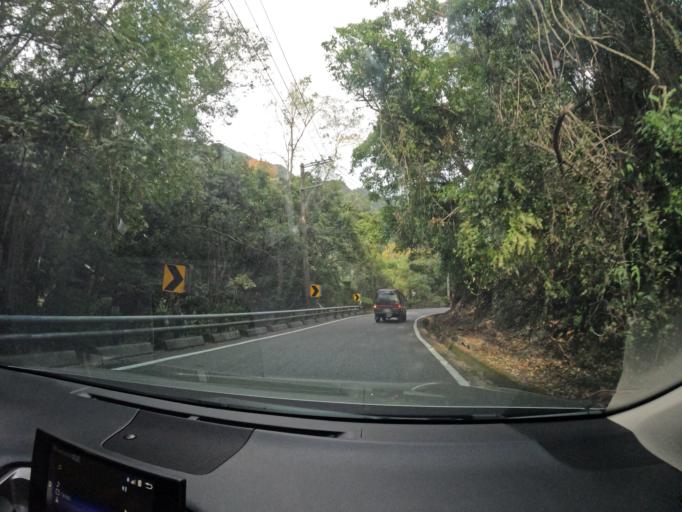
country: TW
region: Taiwan
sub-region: Taitung
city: Taitung
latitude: 23.1415
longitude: 121.0935
